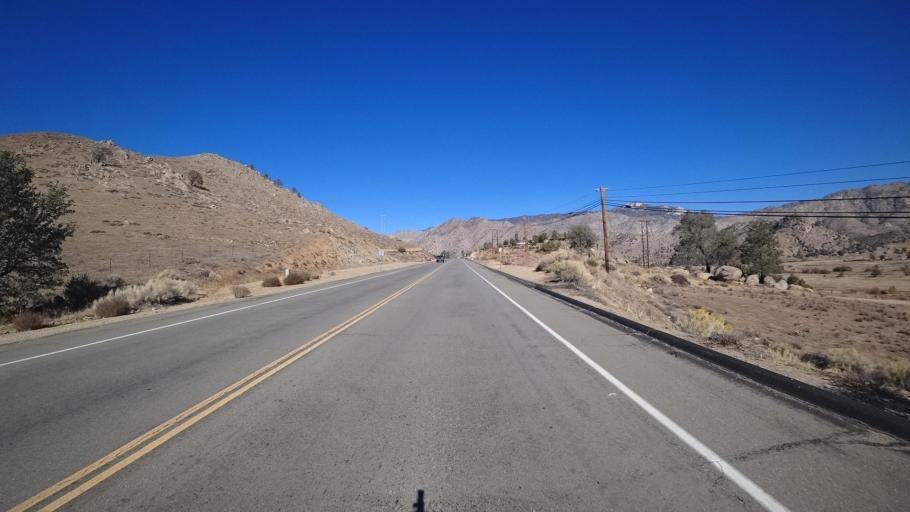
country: US
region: California
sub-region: Kern County
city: Kernville
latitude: 35.7262
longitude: -118.4315
